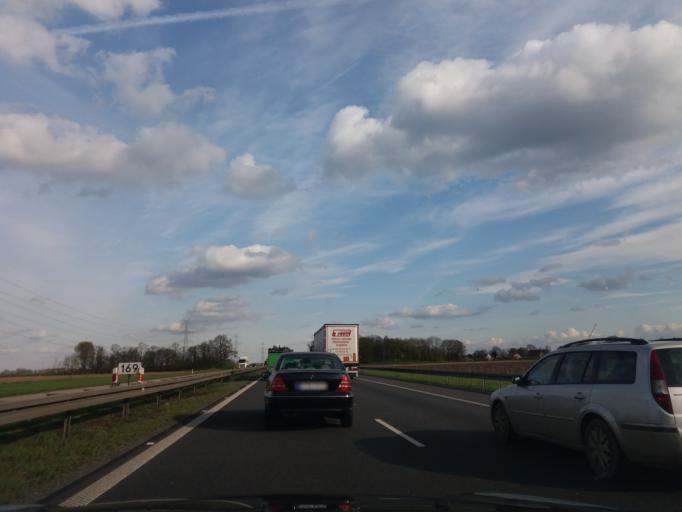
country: PL
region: Lower Silesian Voivodeship
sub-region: Powiat wroclawski
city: Zorawina
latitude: 50.9401
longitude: 17.1022
